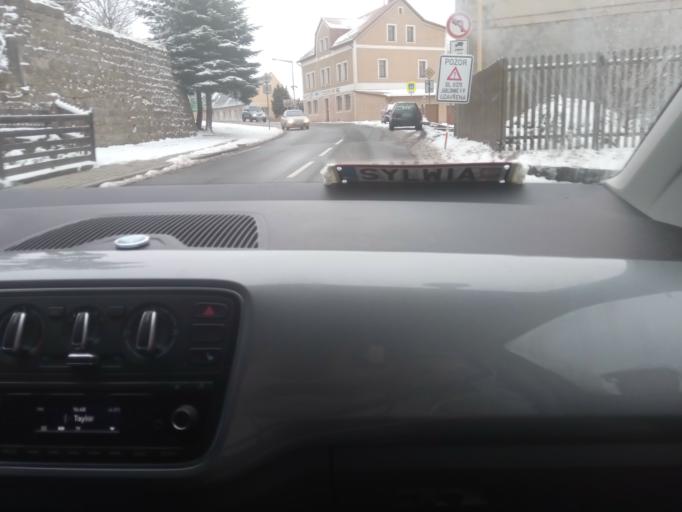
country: CZ
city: Jablonne v Podjestedi
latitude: 50.7646
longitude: 14.7587
